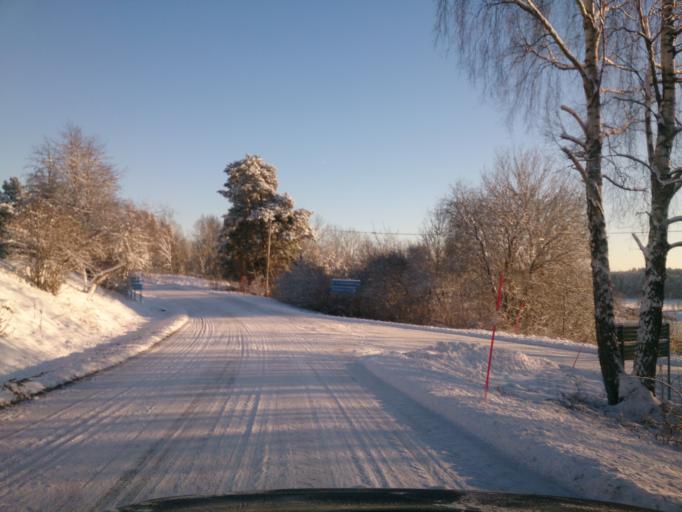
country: SE
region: OEstergoetland
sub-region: Norrkopings Kommun
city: Krokek
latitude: 58.4939
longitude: 16.5533
